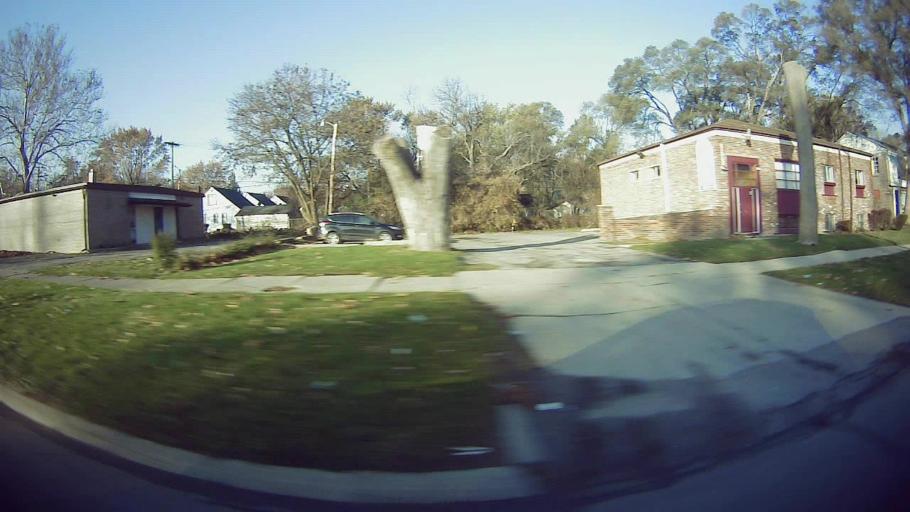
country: US
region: Michigan
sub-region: Oakland County
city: Oak Park
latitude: 42.4237
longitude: -83.1997
